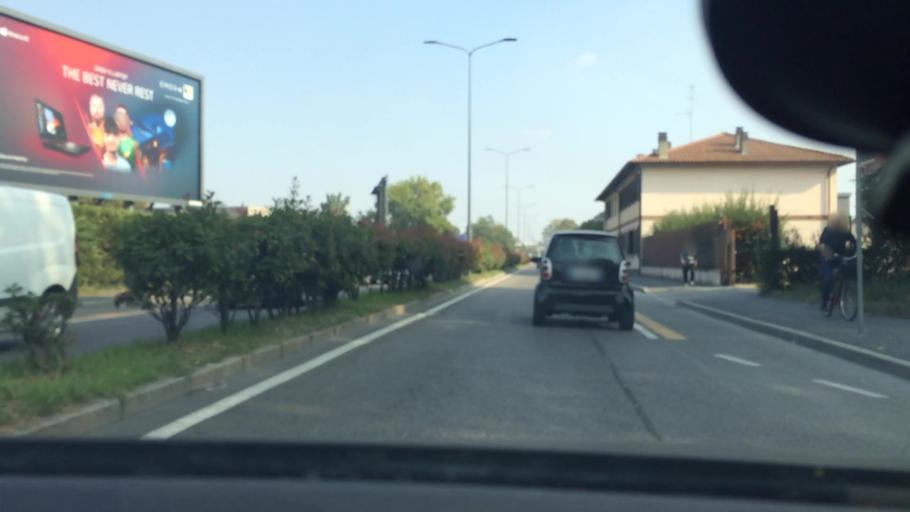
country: IT
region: Lombardy
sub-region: Citta metropolitana di Milano
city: Baranzate
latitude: 45.5031
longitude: 9.1130
